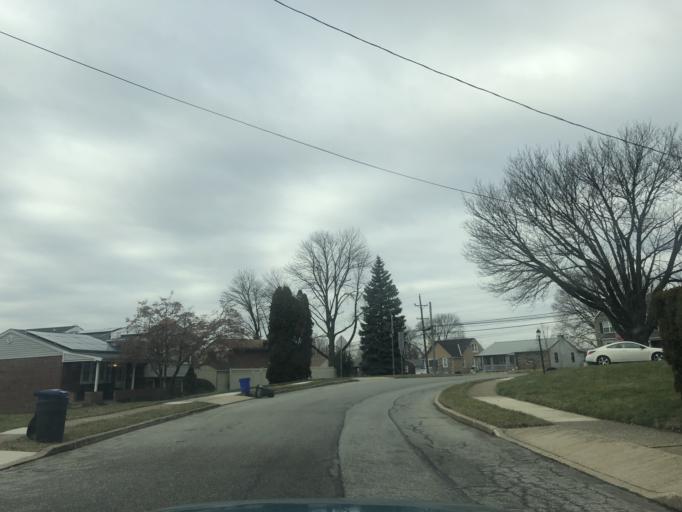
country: US
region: Pennsylvania
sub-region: Montgomery County
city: Conshohocken
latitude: 40.0905
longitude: -75.3010
